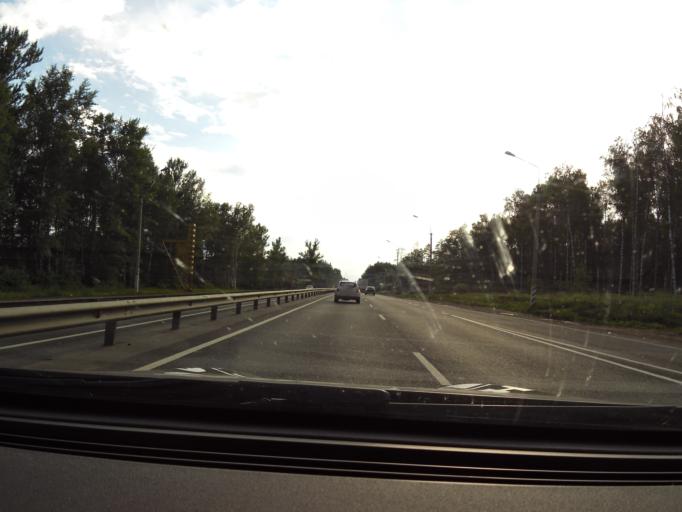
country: RU
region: Vladimir
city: Novki
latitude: 56.2015
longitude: 41.0953
